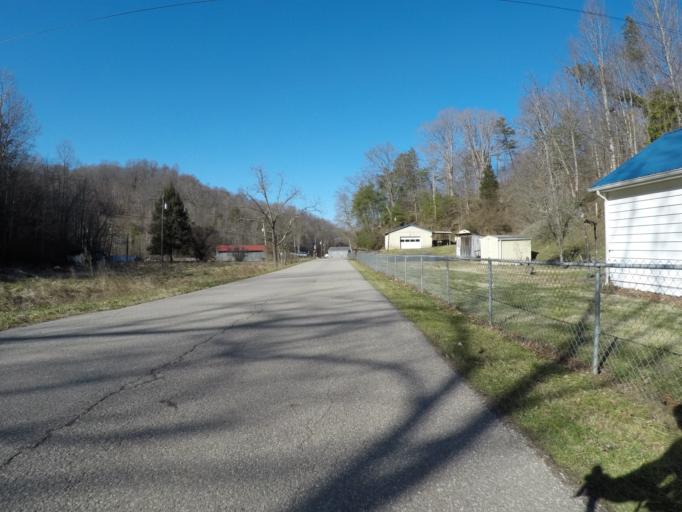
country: US
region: Kentucky
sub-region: Boyd County
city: Catlettsburg
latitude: 38.4098
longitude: -82.6386
